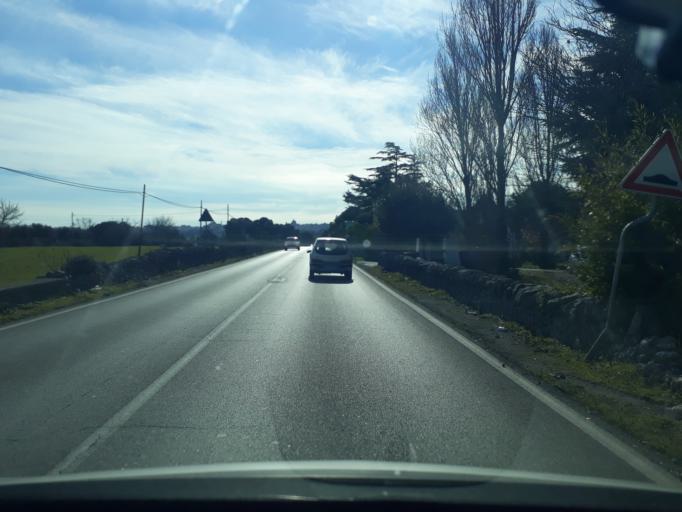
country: IT
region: Apulia
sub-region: Provincia di Taranto
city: Martina Franca
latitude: 40.7274
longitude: 17.3326
